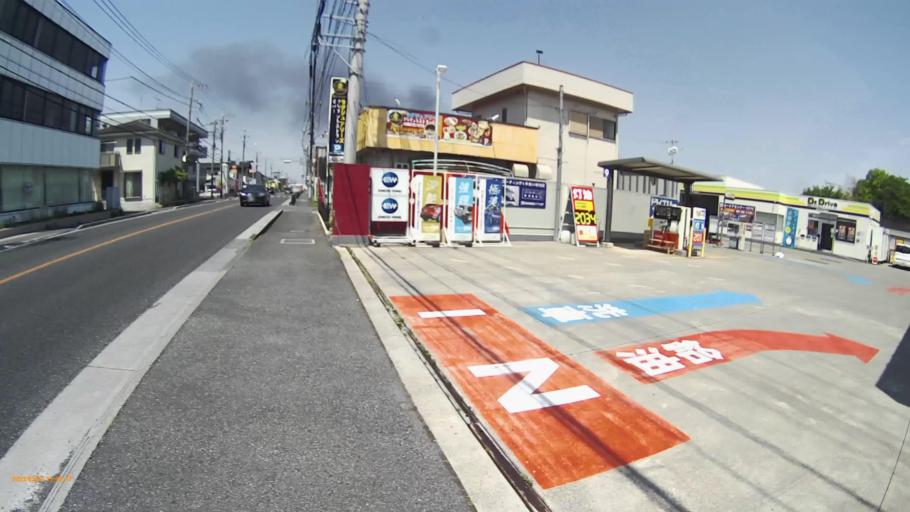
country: JP
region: Saitama
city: Kasukabe
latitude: 35.9517
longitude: 139.7762
